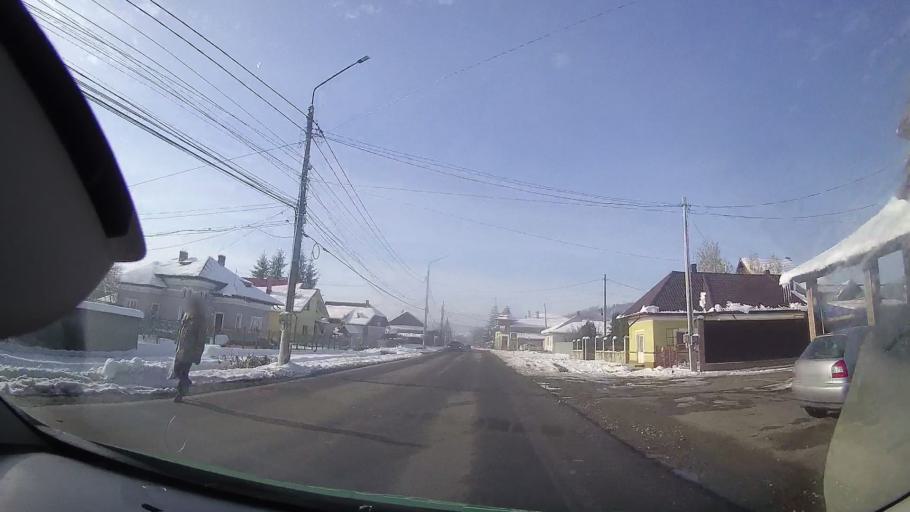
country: RO
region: Neamt
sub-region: Oras Targu Neamt
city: Targu Neamt
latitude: 47.2086
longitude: 26.3870
